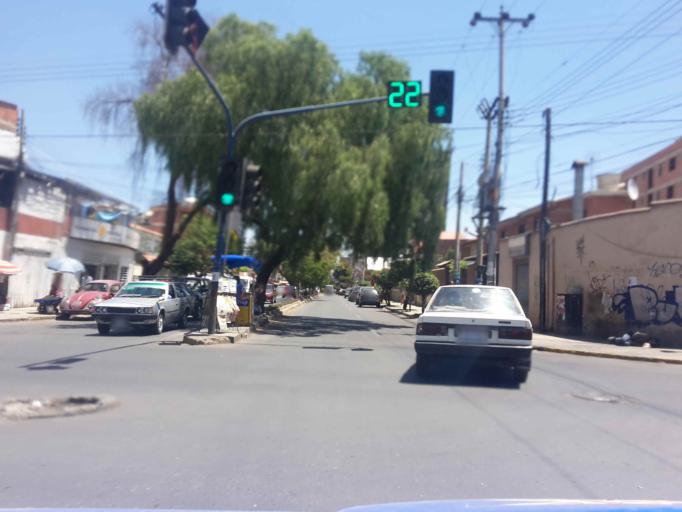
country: BO
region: Cochabamba
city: Cochabamba
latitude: -17.3843
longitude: -66.1462
